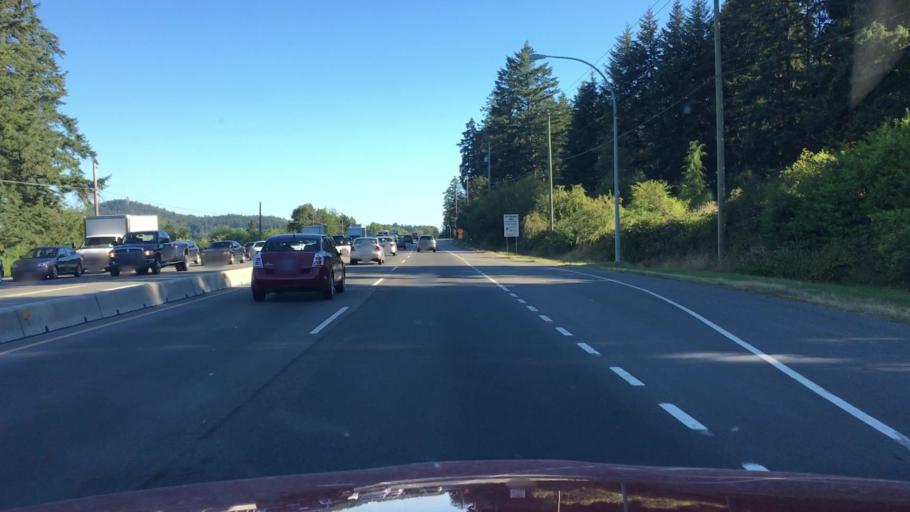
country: CA
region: British Columbia
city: Victoria
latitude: 48.5186
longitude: -123.3851
